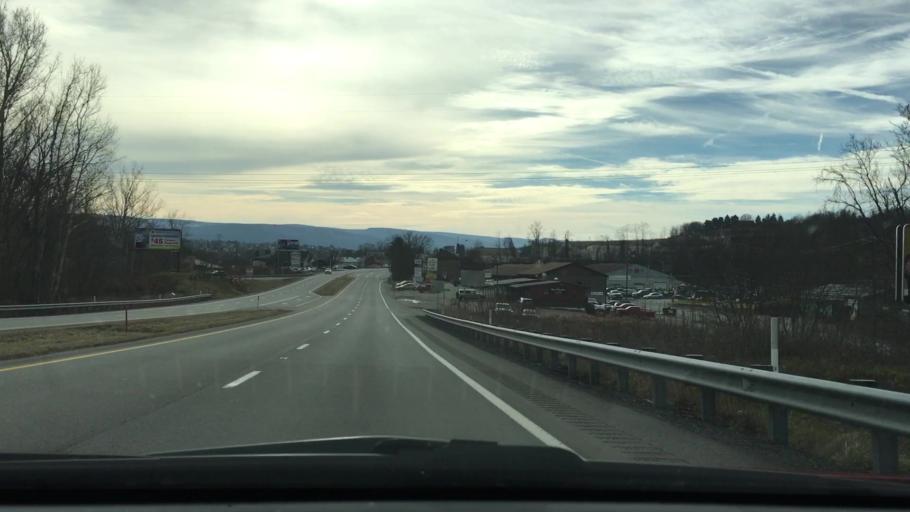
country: US
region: Pennsylvania
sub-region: Fayette County
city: Oliver
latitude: 39.9295
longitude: -79.7282
